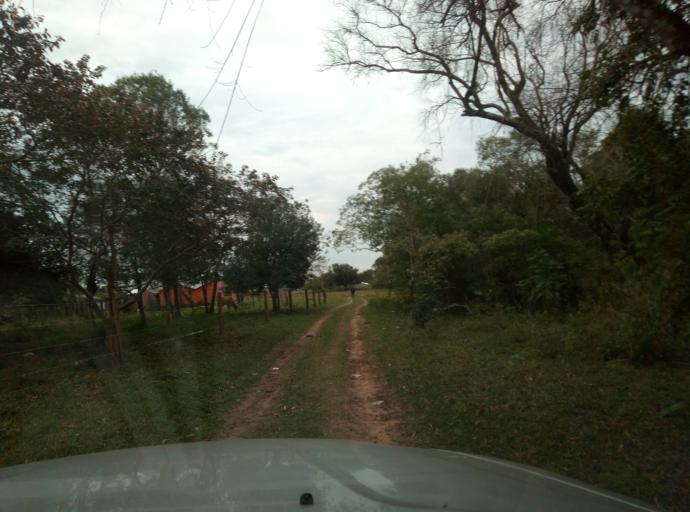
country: PY
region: Caaguazu
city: Carayao
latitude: -25.1625
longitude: -56.3334
